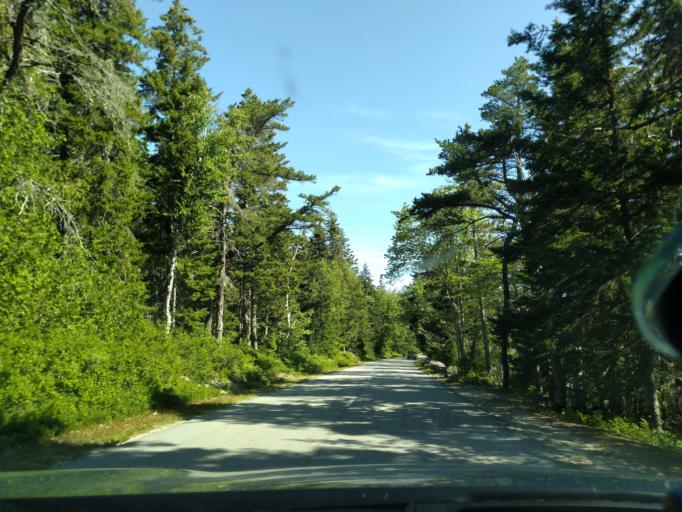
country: US
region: Maine
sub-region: Hancock County
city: Gouldsboro
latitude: 44.3591
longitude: -68.0469
